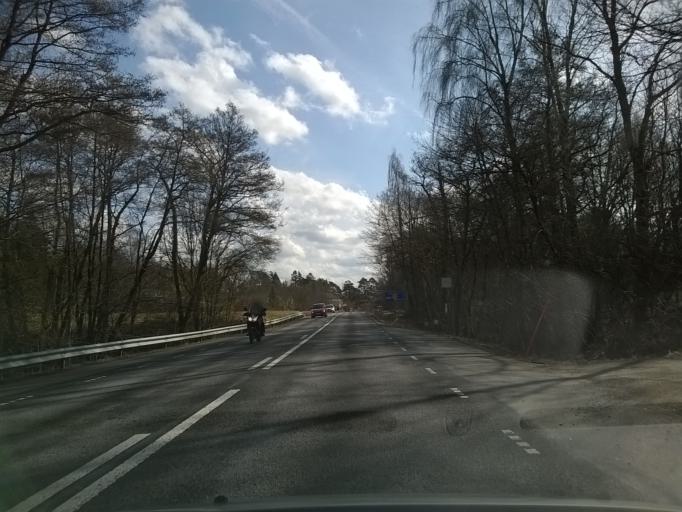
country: SE
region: Vaestra Goetaland
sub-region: Orust
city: Henan
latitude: 58.3172
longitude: 11.6841
